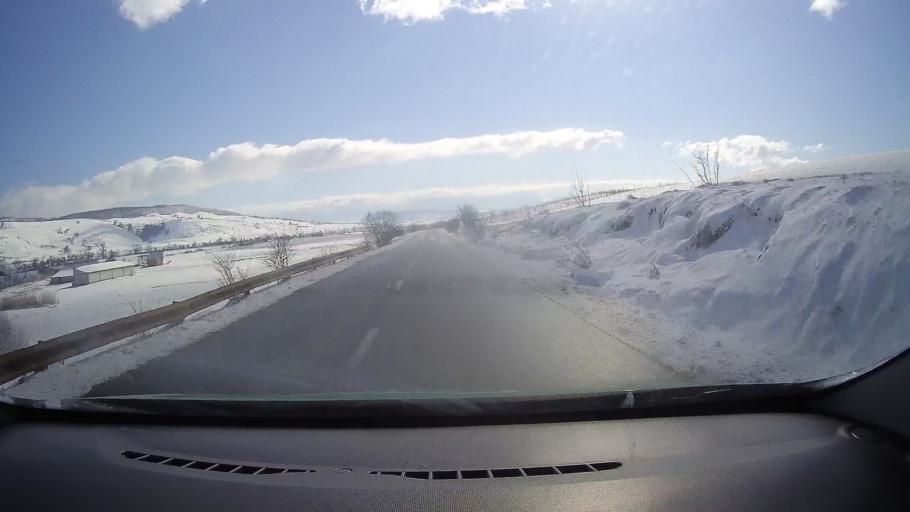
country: RO
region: Sibiu
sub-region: Comuna Rosia
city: Rosia
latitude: 45.8321
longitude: 24.3112
